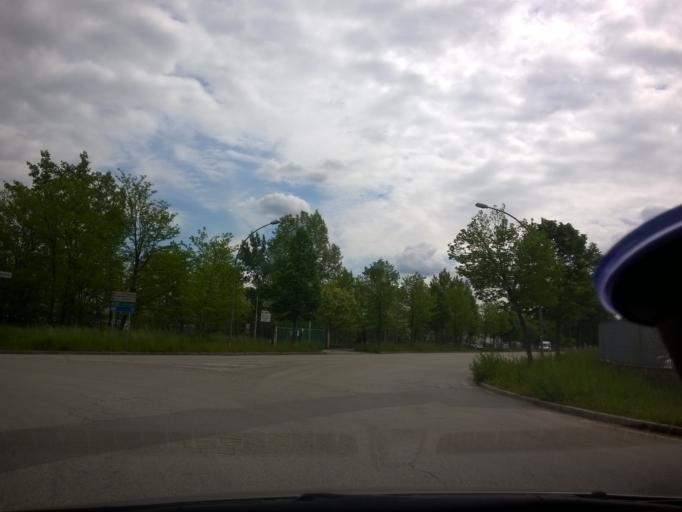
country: IT
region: Veneto
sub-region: Provincia di Treviso
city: Scomigo
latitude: 45.9499
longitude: 12.3203
